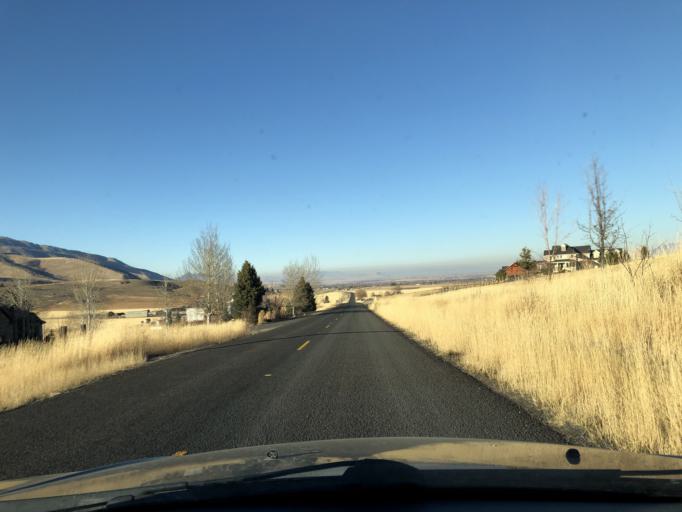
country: US
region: Utah
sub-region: Cache County
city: Wellsville
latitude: 41.5829
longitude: -111.9253
